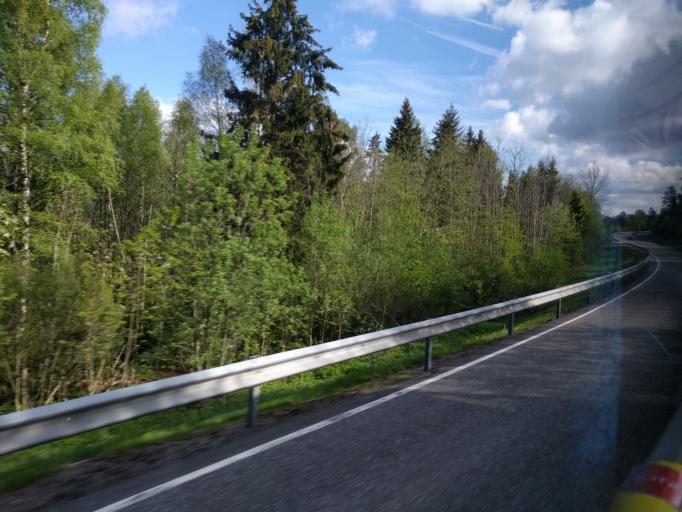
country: NO
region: Vestfold
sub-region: Lardal
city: Svarstad
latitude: 59.3614
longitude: 9.9155
